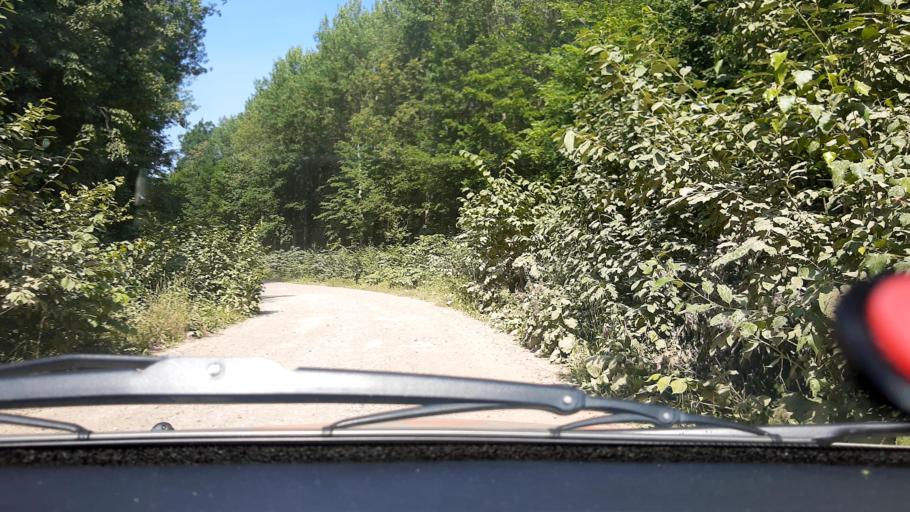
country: RU
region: Bashkortostan
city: Karmaskaly
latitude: 54.3869
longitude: 55.8922
